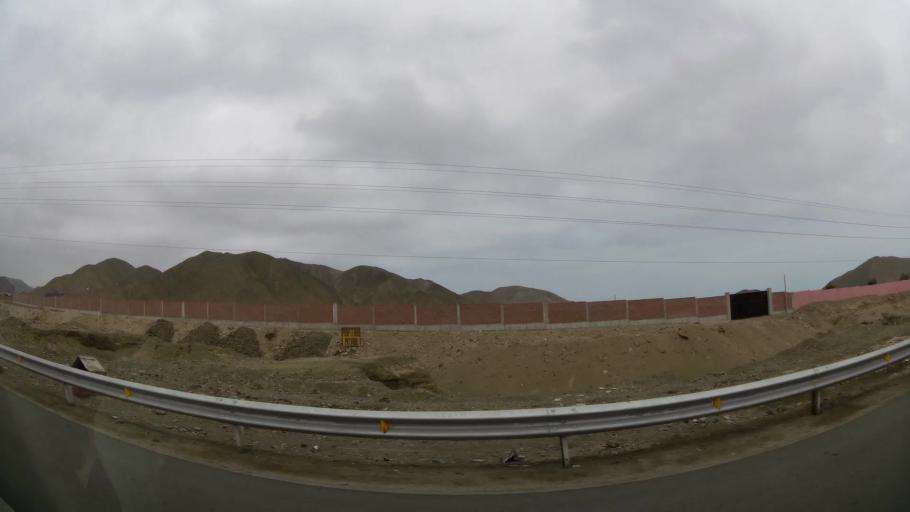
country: PE
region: Lima
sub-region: Lima
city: San Bartolo
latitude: -12.3977
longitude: -76.7575
